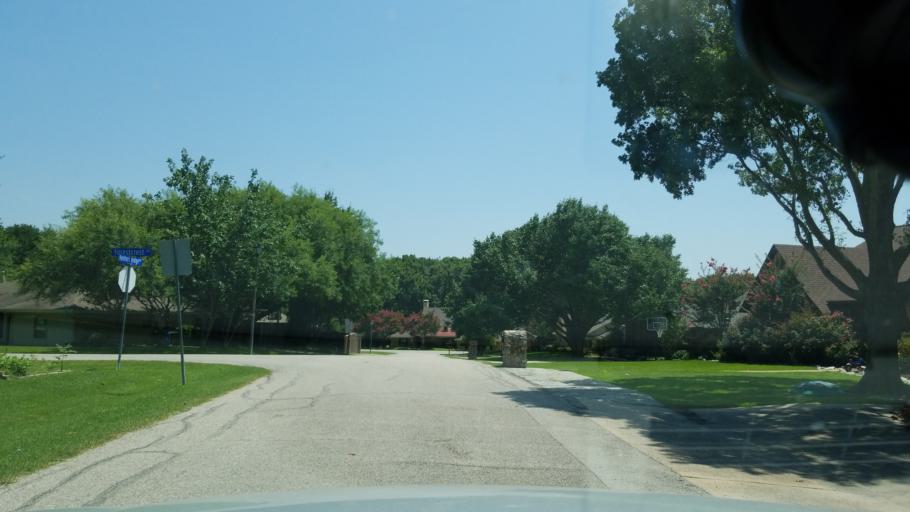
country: US
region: Texas
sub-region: Dallas County
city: Coppell
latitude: 32.9574
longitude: -96.9878
